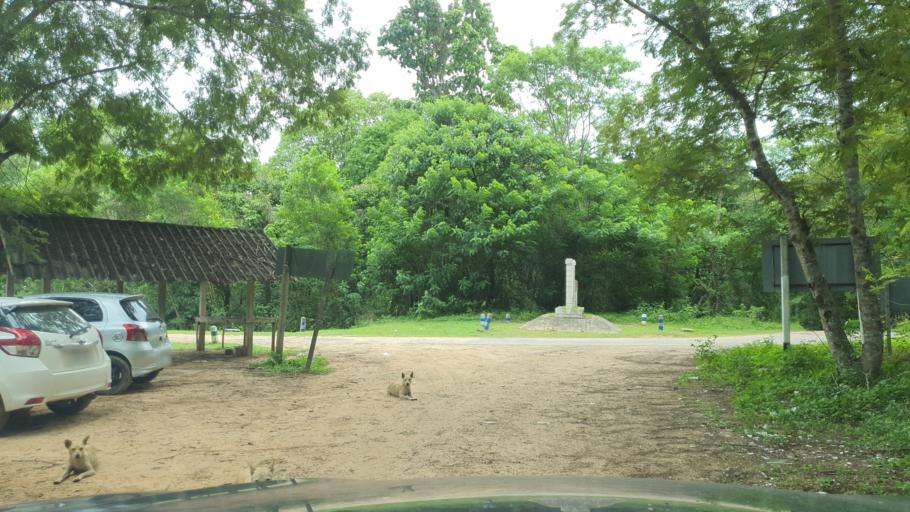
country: TH
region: Chiang Mai
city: Mae On
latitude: 18.6856
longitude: 99.2046
